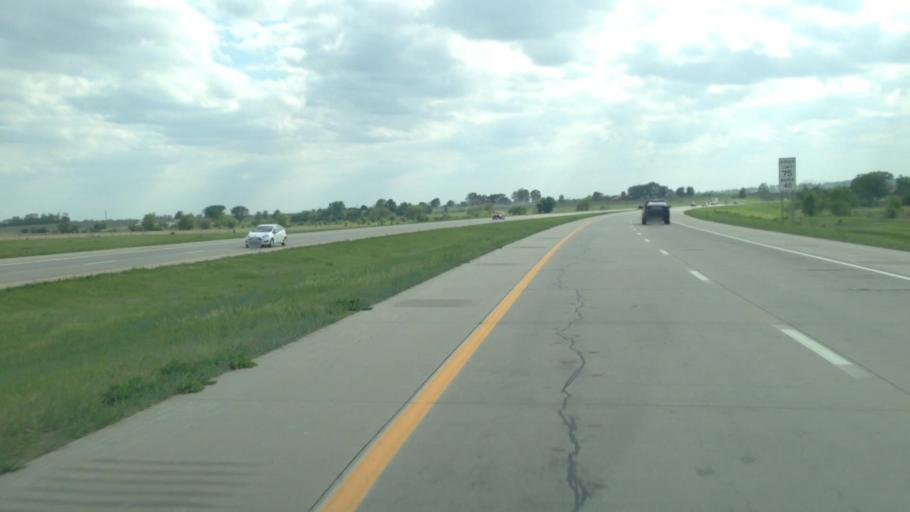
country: US
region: Kansas
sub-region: Franklin County
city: Ottawa
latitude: 38.5865
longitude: -95.2397
